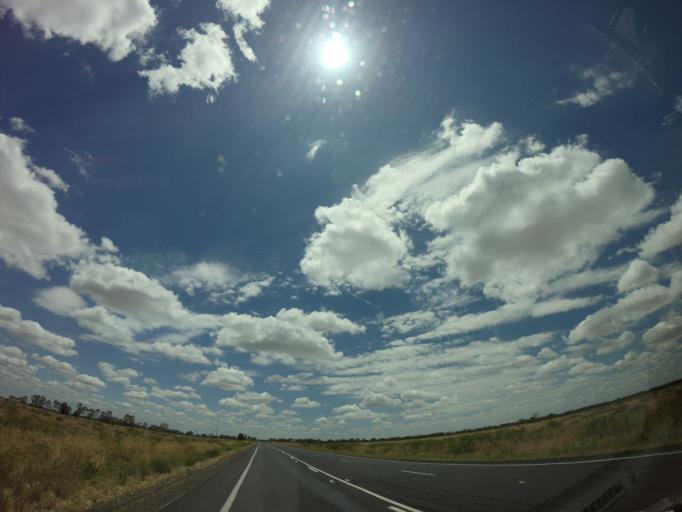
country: AU
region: New South Wales
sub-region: Moree Plains
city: Boggabilla
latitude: -28.9363
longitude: 150.1068
